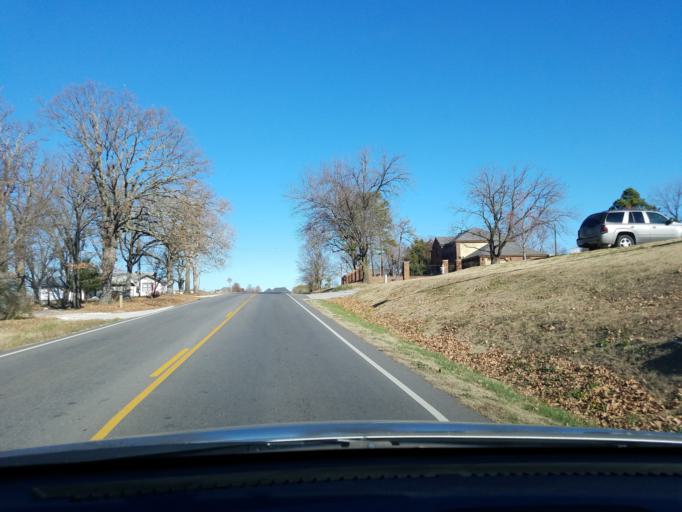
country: US
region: Arkansas
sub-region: Carroll County
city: Berryville
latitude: 36.3822
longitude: -93.5673
